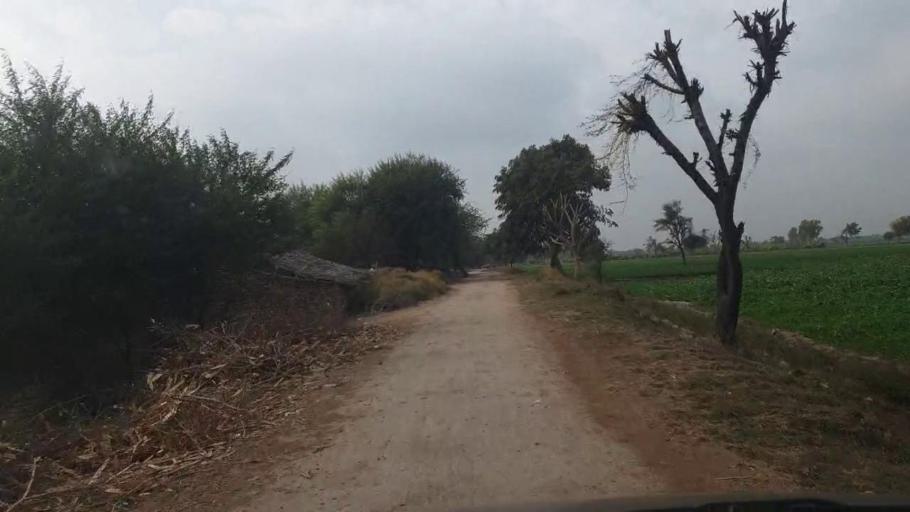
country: PK
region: Sindh
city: Shahdadpur
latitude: 25.9450
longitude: 68.7219
